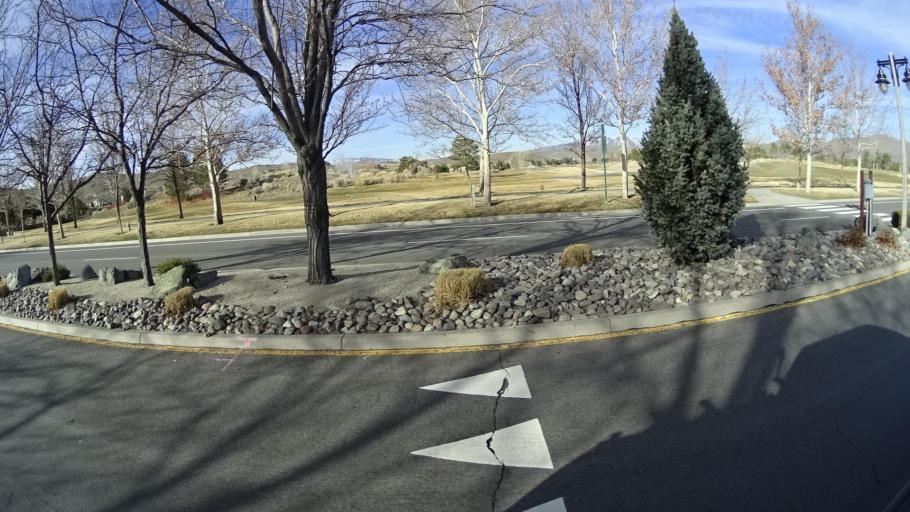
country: US
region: Nevada
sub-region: Washoe County
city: Spanish Springs
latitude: 39.6081
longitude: -119.6863
